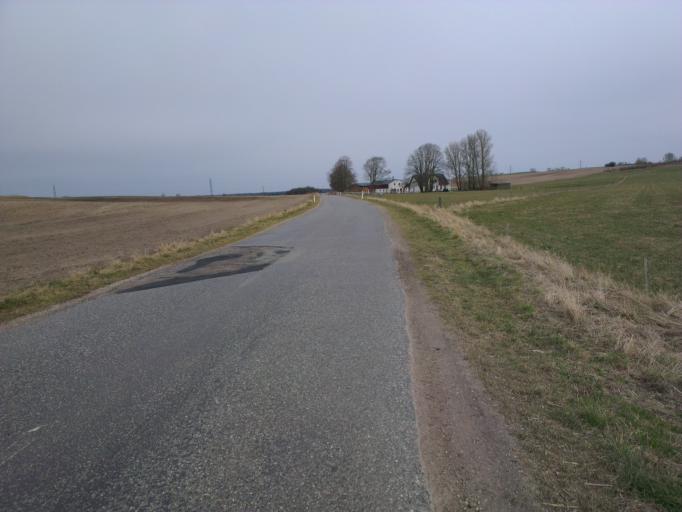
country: DK
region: Capital Region
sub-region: Frederikssund Kommune
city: Skibby
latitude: 55.7965
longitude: 11.9234
